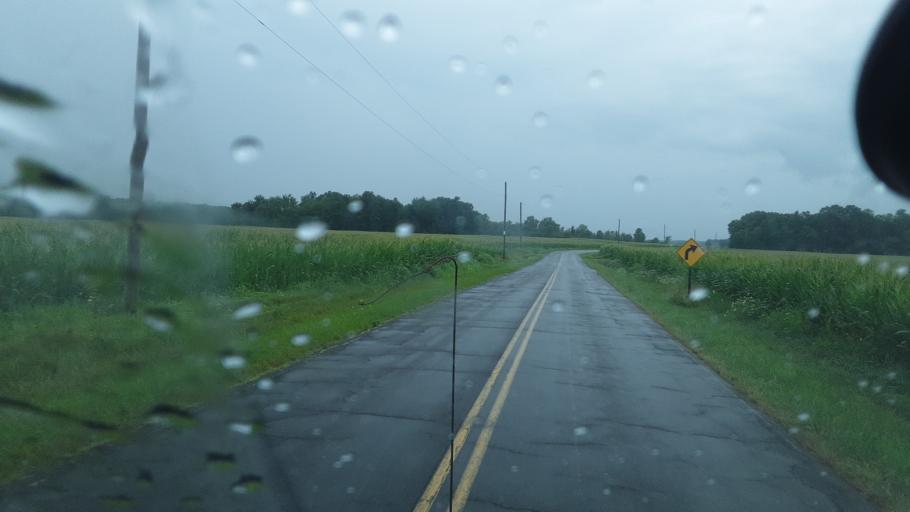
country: US
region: Ohio
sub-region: Williams County
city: Edgerton
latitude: 41.4974
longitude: -84.7896
